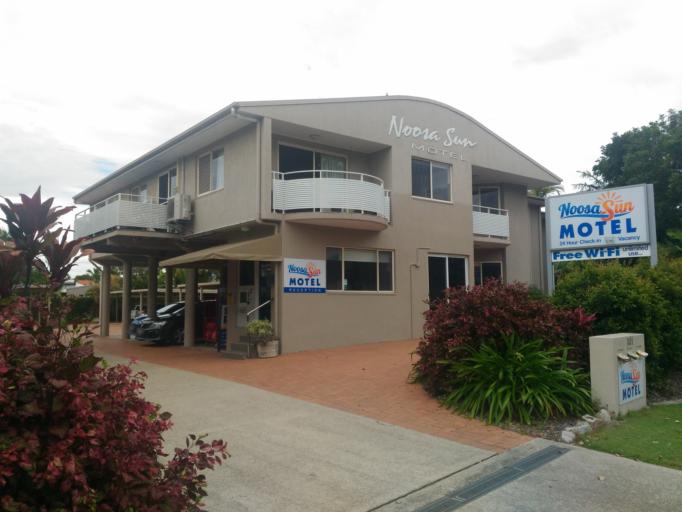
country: AU
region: Queensland
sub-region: Sunshine Coast
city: Noosaville
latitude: -26.3983
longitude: 153.0558
